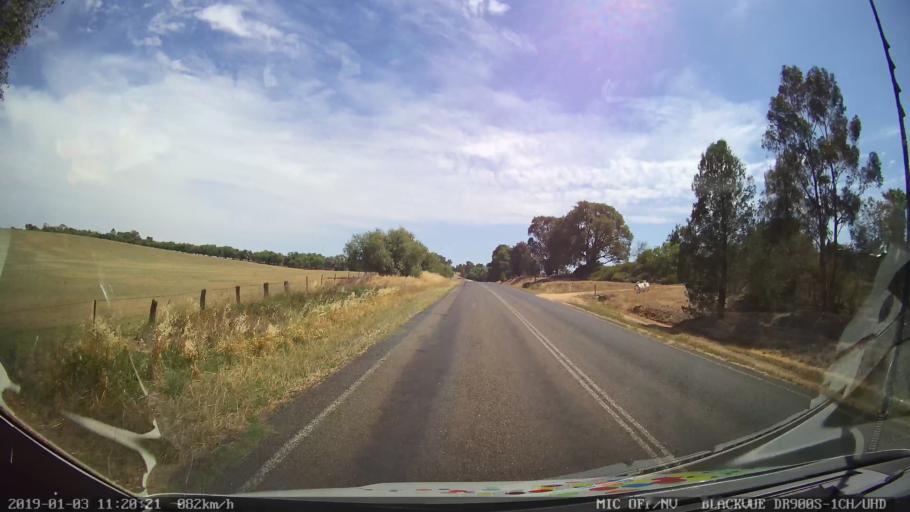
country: AU
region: New South Wales
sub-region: Young
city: Young
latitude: -34.1021
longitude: 148.2549
